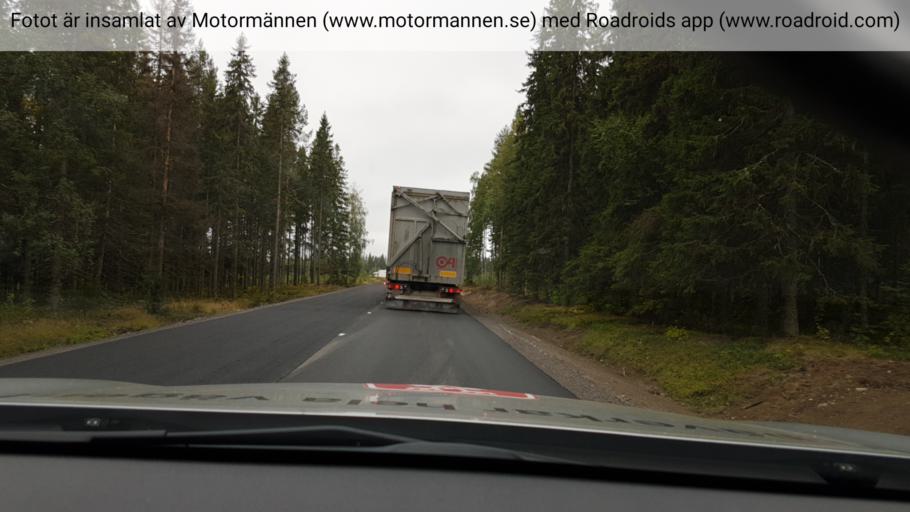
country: SE
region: Vaesterbotten
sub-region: Skelleftea Kommun
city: Burtraesk
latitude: 64.4075
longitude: 20.5449
